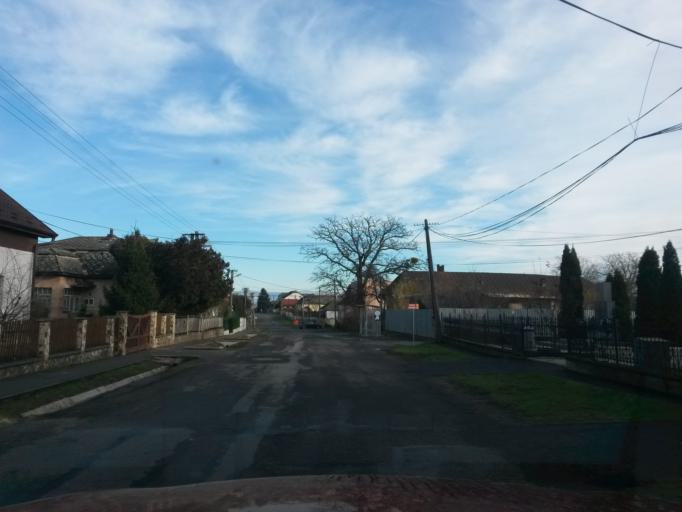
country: SK
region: Kosicky
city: Cierna nad Tisou
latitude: 48.5396
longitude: 22.0247
